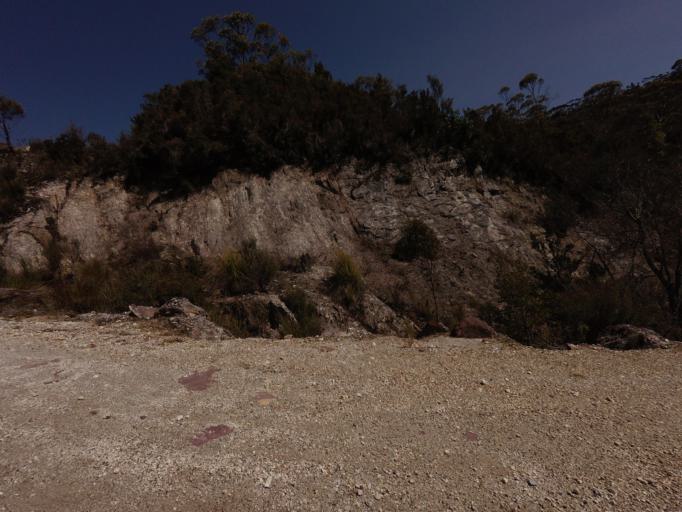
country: AU
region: Tasmania
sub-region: Huon Valley
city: Geeveston
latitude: -43.0407
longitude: 146.2762
